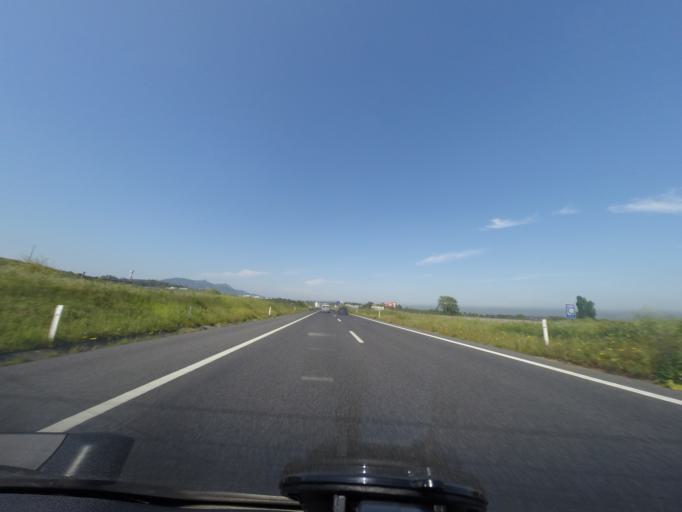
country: PT
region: Lisbon
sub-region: Sintra
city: Sintra
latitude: 38.8152
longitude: -9.3473
